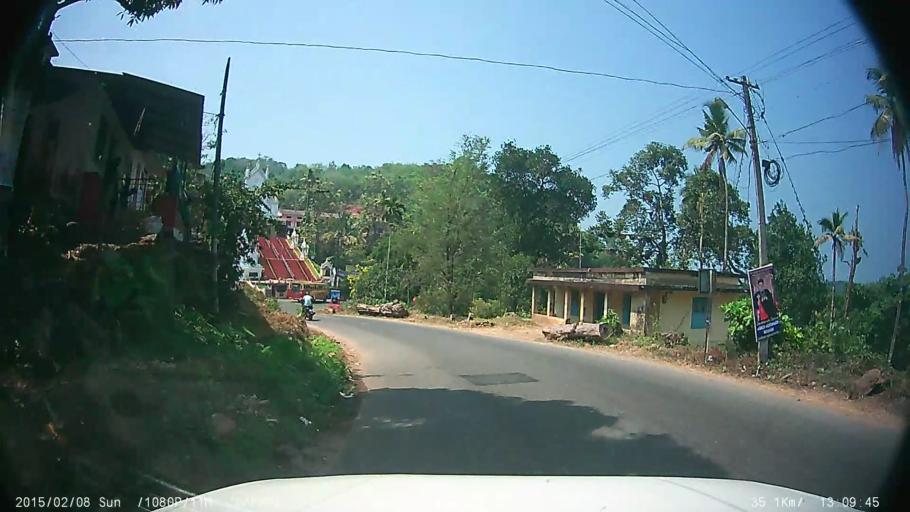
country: IN
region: Kerala
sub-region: Ernakulam
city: Muvattupuzha
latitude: 9.9288
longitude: 76.5782
